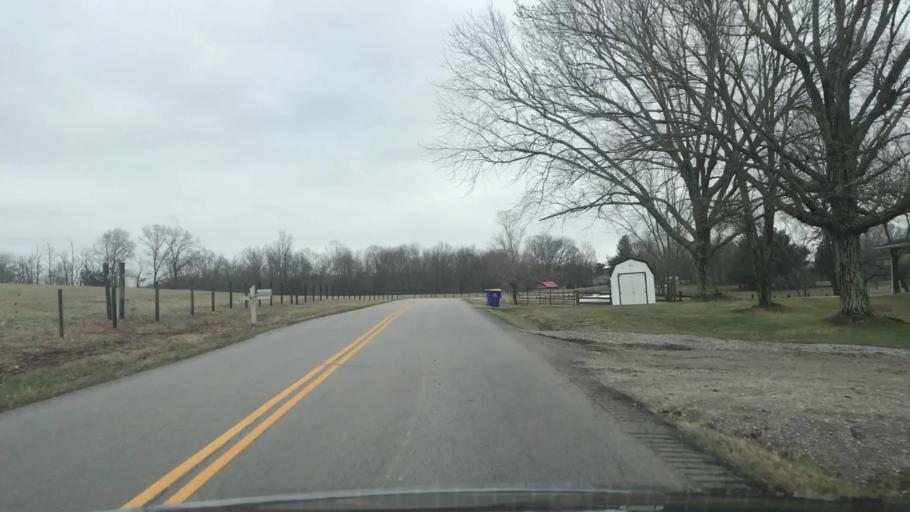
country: US
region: Kentucky
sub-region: Barren County
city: Glasgow
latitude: 36.9116
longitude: -85.8000
